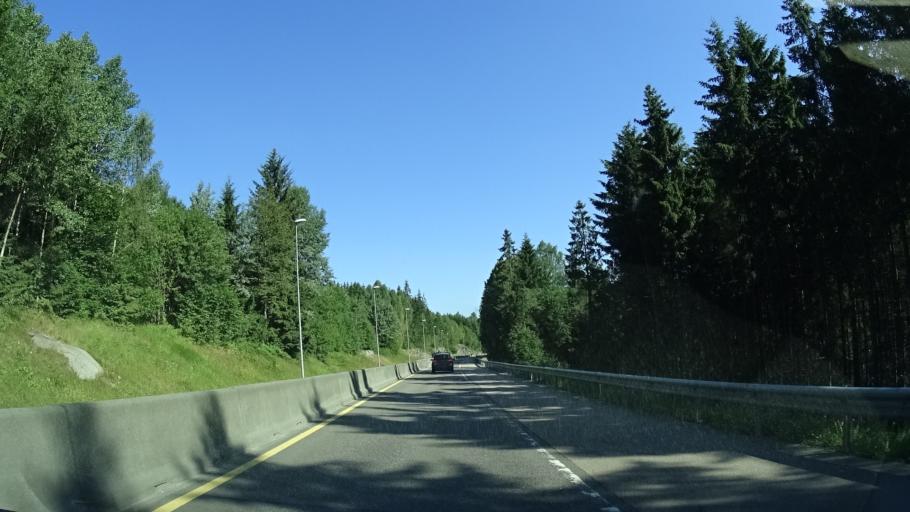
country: NO
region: Akershus
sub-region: Ski
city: Ski
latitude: 59.7351
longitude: 10.7828
